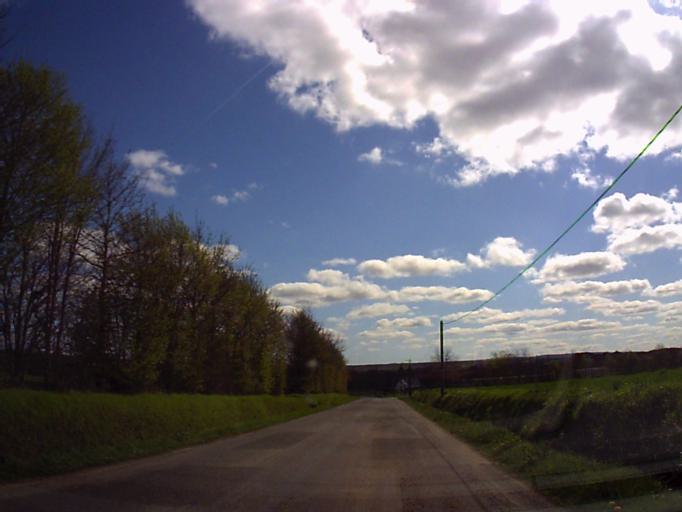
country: FR
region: Brittany
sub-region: Departement d'Ille-et-Vilaine
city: Saint-Meen-le-Grand
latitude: 48.1366
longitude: -2.1578
